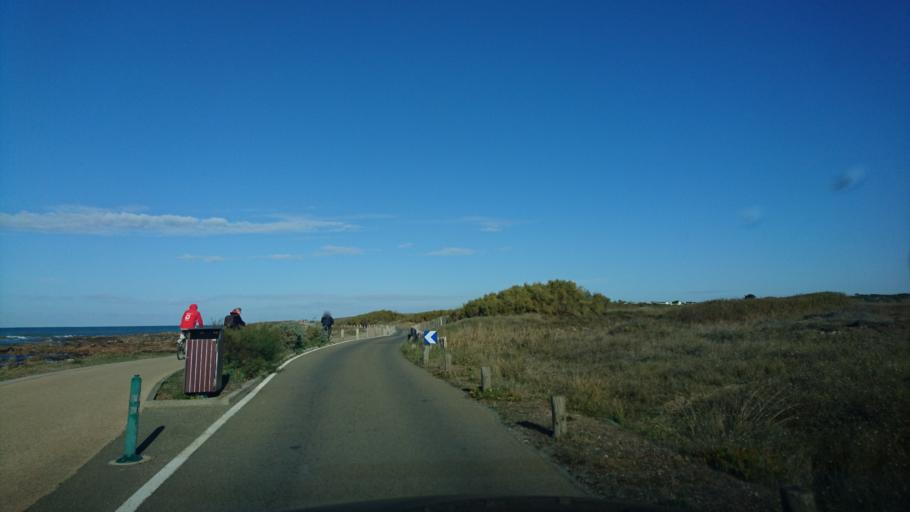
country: FR
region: Pays de la Loire
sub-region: Departement de la Vendee
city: Les Sables-d'Olonne
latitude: 46.5072
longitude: -1.8170
